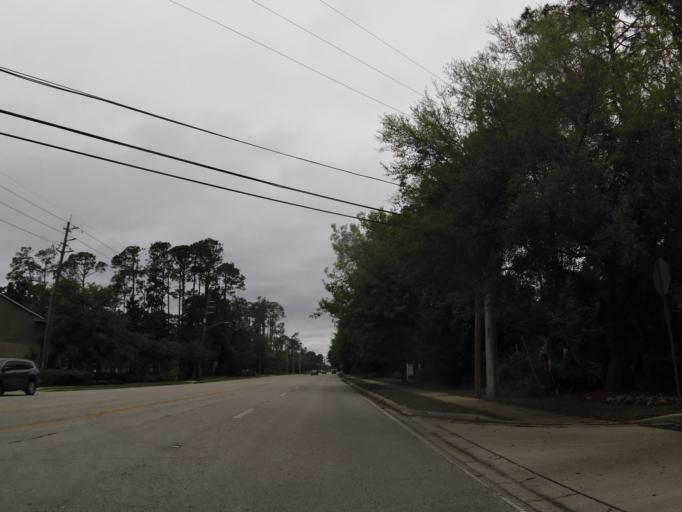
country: US
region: Florida
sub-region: Saint Johns County
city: Fruit Cove
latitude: 30.1933
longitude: -81.6104
